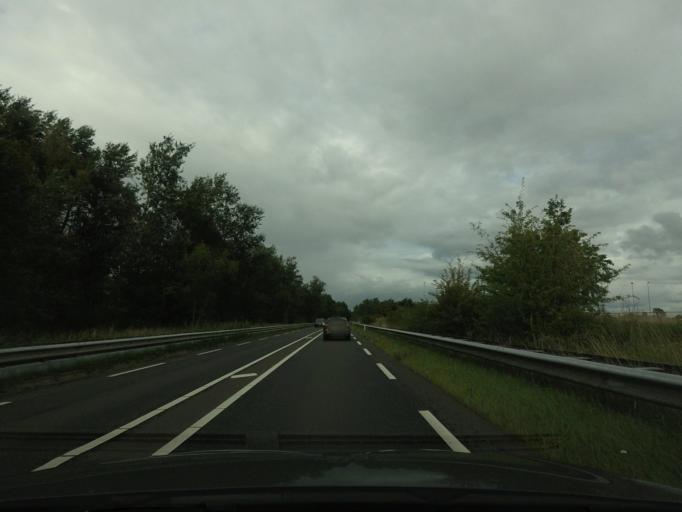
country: NL
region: South Holland
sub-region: Gemeente Hillegom
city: Hillegom
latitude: 52.3063
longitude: 4.5415
